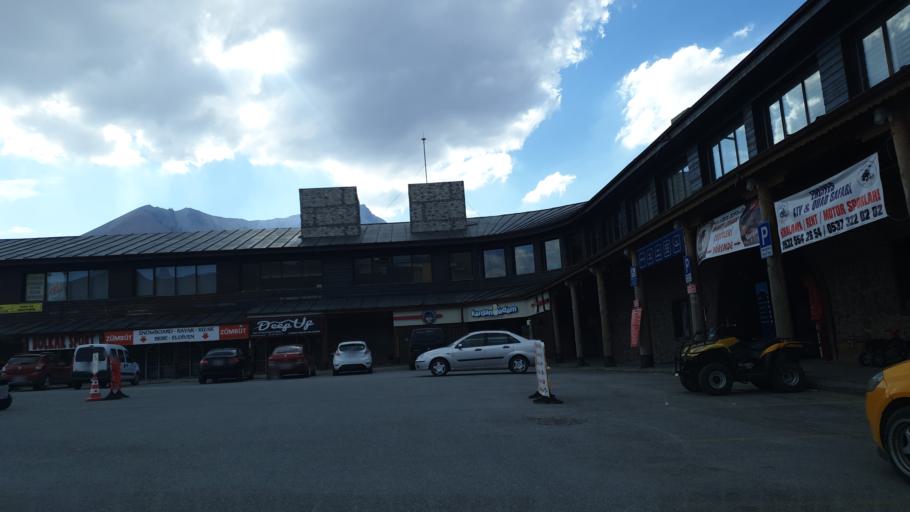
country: TR
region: Kayseri
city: Hacilar
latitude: 38.5401
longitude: 35.5272
